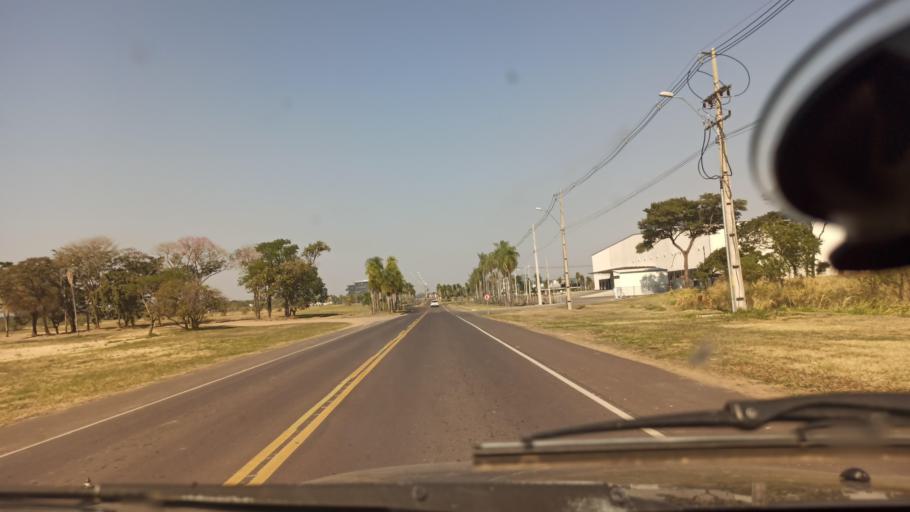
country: PY
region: Central
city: Colonia Mariano Roque Alonso
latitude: -25.1948
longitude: -57.5710
